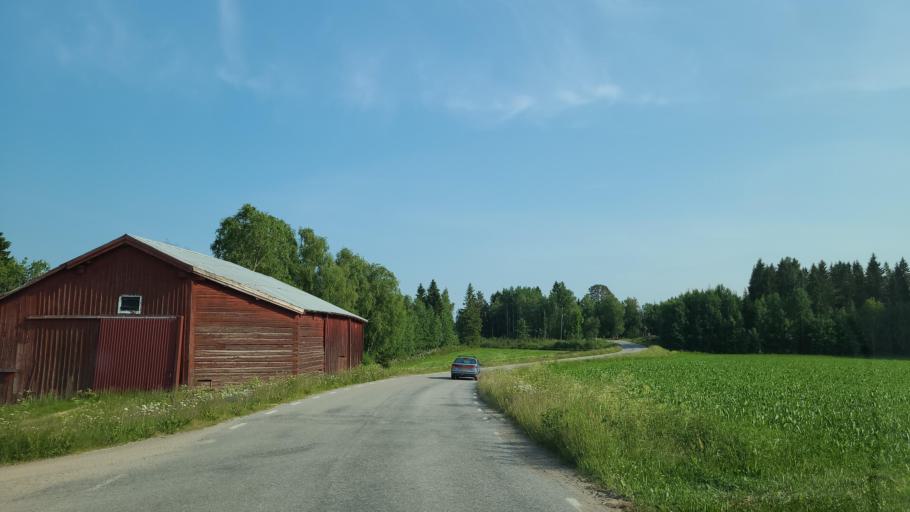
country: SE
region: Vaesterbotten
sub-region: Skelleftea Kommun
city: Burea
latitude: 64.3472
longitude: 21.3393
